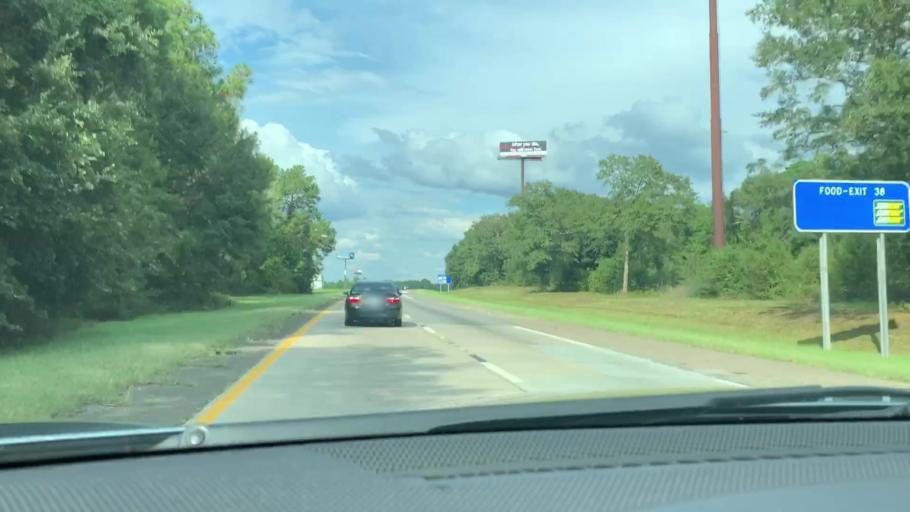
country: US
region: South Carolina
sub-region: Hampton County
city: Yemassee
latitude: 32.6925
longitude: -80.8792
